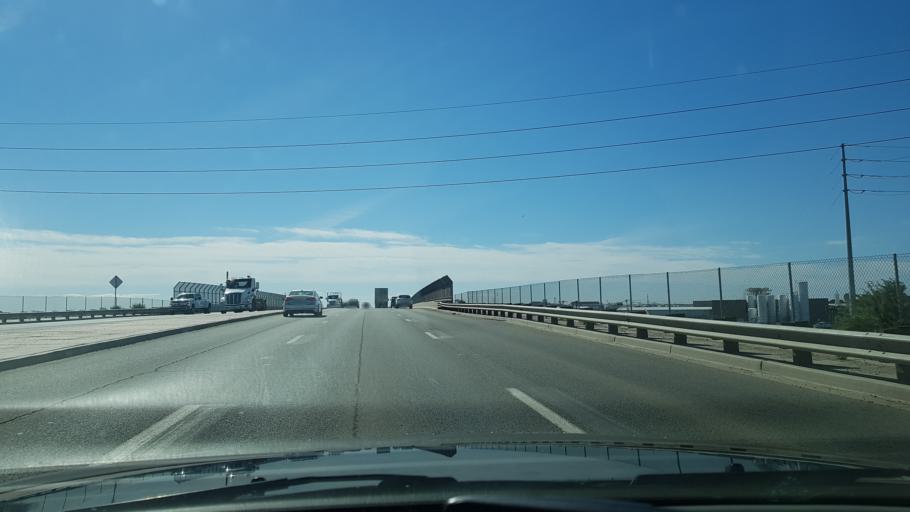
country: US
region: Arizona
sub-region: Yuma County
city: Yuma
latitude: 32.6852
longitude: -114.5816
